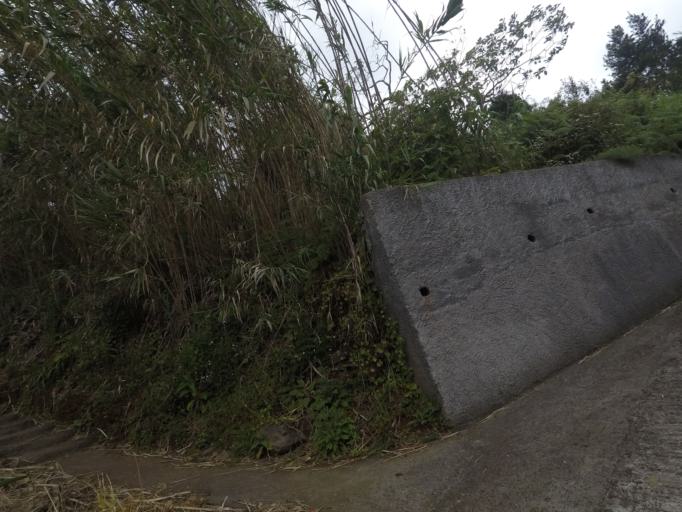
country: PT
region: Madeira
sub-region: Santana
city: Santana
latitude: 32.8019
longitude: -16.8727
